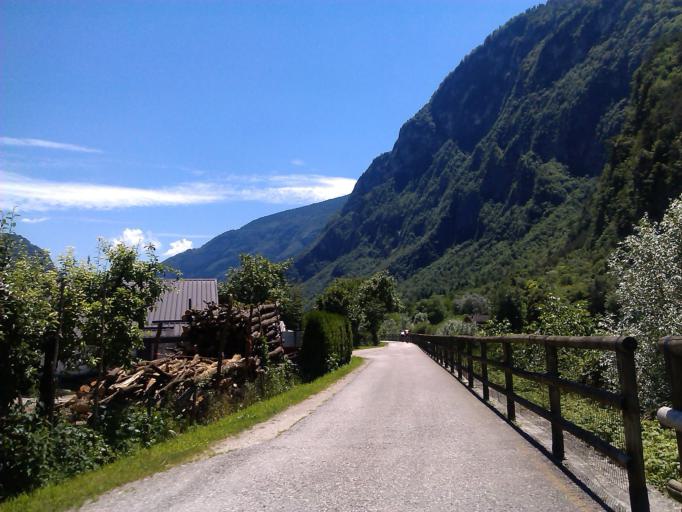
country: IT
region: Trentino-Alto Adige
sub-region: Provincia di Trento
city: Grigno
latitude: 45.9919
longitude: 11.6644
